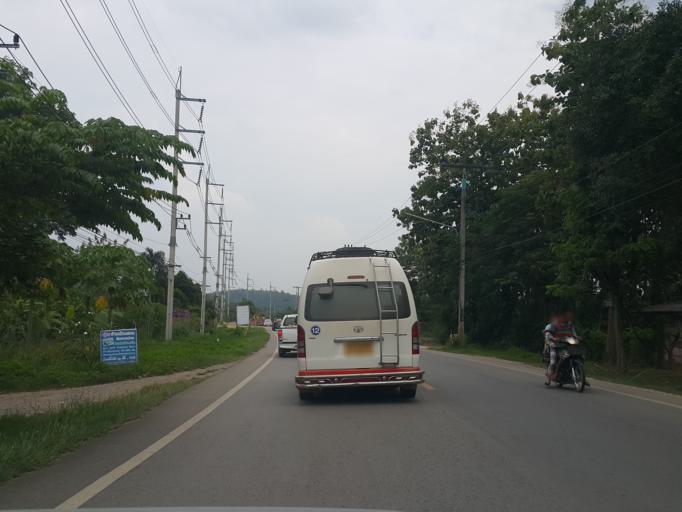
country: TH
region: Chiang Mai
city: Mae Taeng
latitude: 19.0911
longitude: 98.8864
